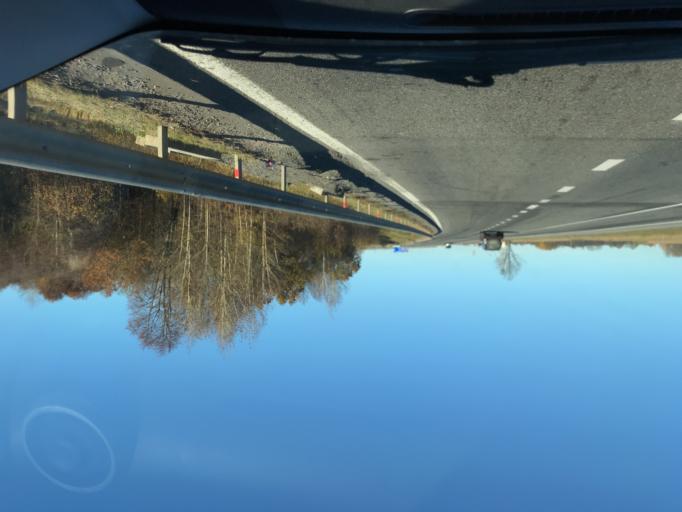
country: BY
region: Vitebsk
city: Vitebsk
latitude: 55.0975
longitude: 30.3005
